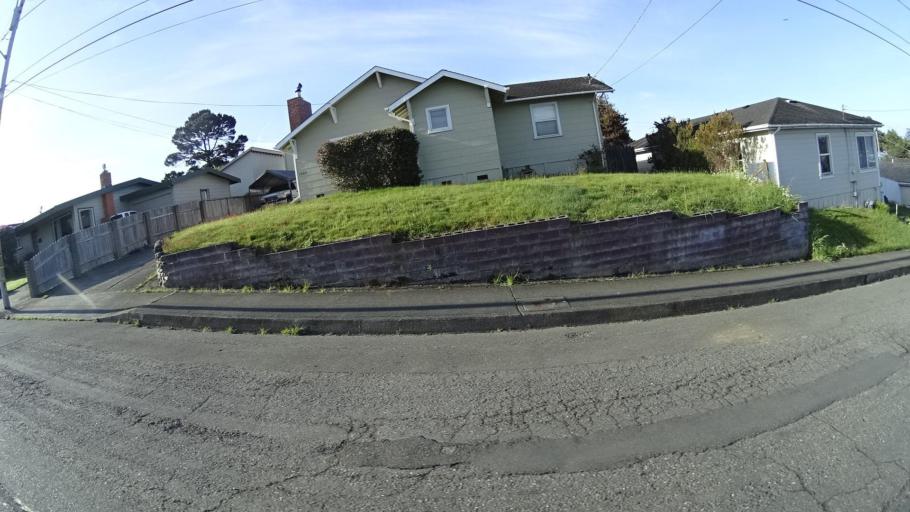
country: US
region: California
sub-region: Humboldt County
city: Bayview
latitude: 40.7741
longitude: -124.1823
